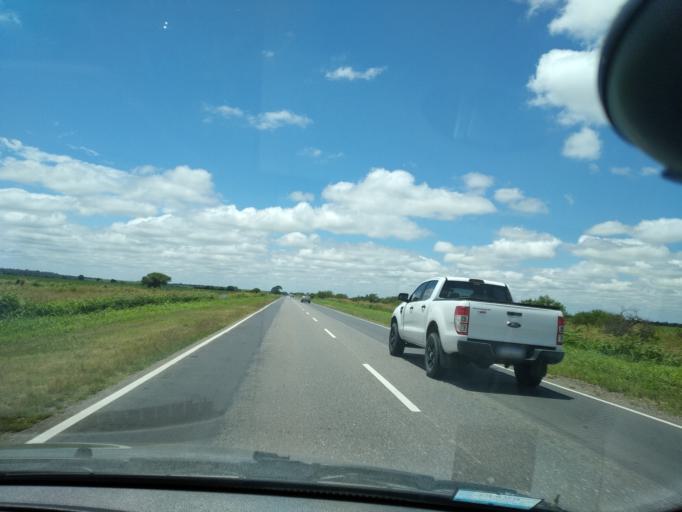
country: AR
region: Cordoba
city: Despenaderos
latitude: -31.6513
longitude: -64.1915
